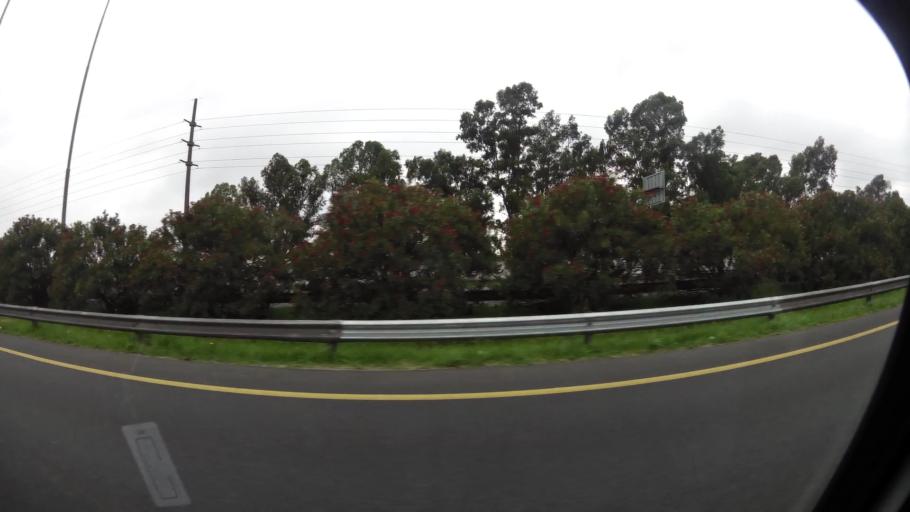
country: AR
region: Buenos Aires
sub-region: Partido de Quilmes
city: Quilmes
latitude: -34.7095
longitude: -58.2567
